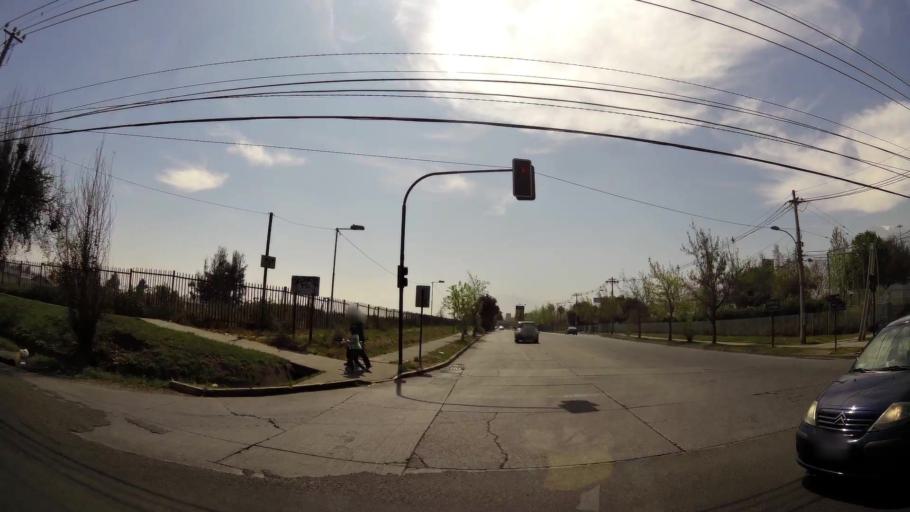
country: CL
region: Santiago Metropolitan
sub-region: Provincia de Santiago
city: Villa Presidente Frei, Nunoa, Santiago, Chile
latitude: -33.4632
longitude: -70.5477
